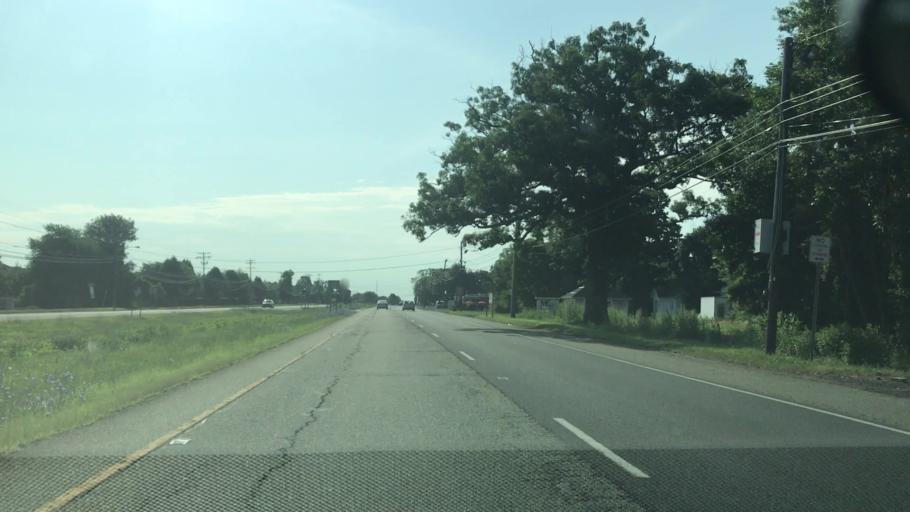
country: US
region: New Jersey
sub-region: Somerset County
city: Bridgewater
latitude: 40.6079
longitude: -74.7069
